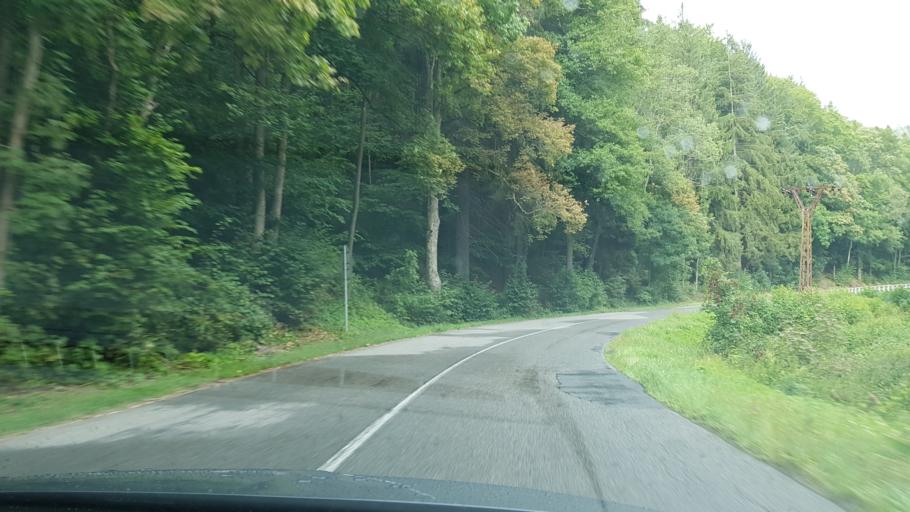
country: CZ
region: Olomoucky
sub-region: Okres Sumperk
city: Hanusovice
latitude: 50.0889
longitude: 16.9157
